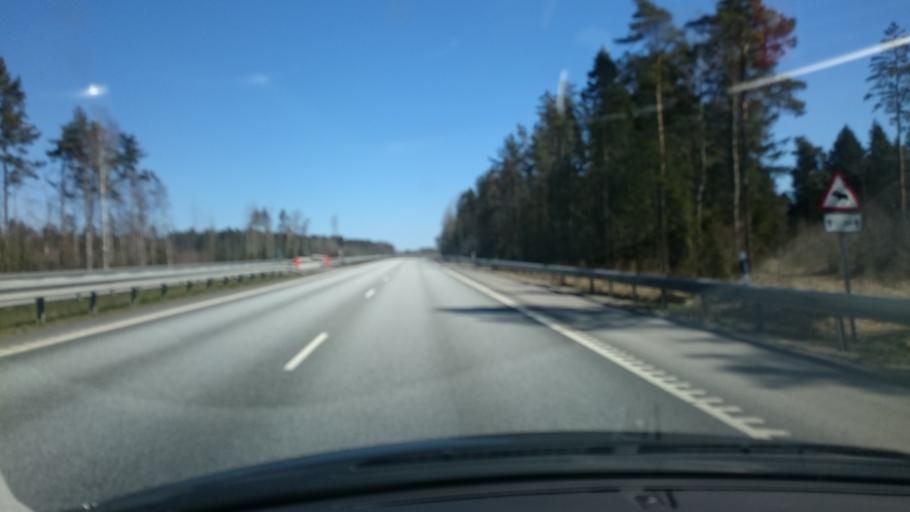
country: EE
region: Harju
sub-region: Kiili vald
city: Kiili
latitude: 59.3278
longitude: 24.7833
